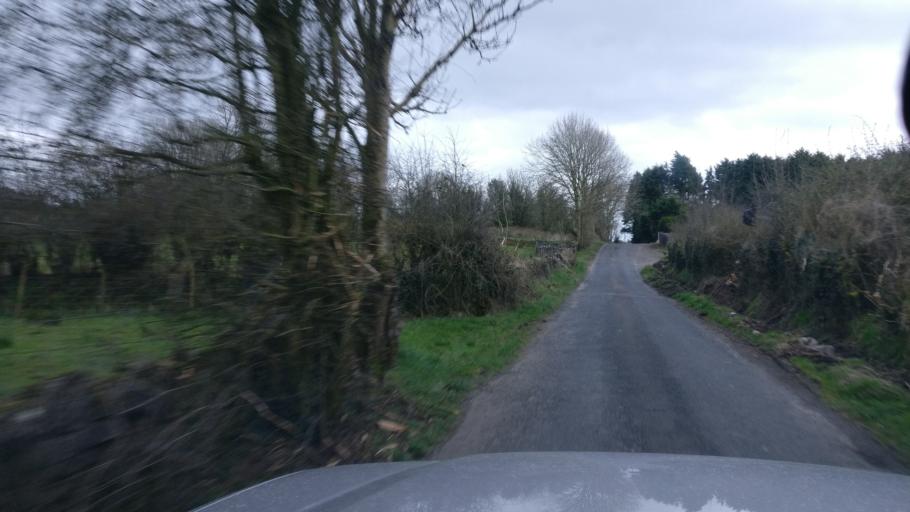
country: IE
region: Connaught
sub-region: County Galway
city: Loughrea
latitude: 53.2613
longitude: -8.4543
